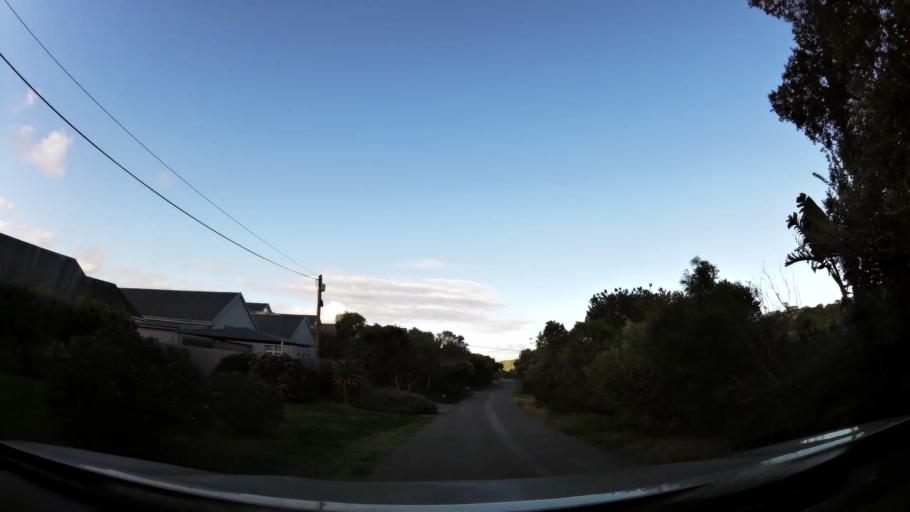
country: ZA
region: Western Cape
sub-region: Eden District Municipality
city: George
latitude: -33.9980
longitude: 22.6265
